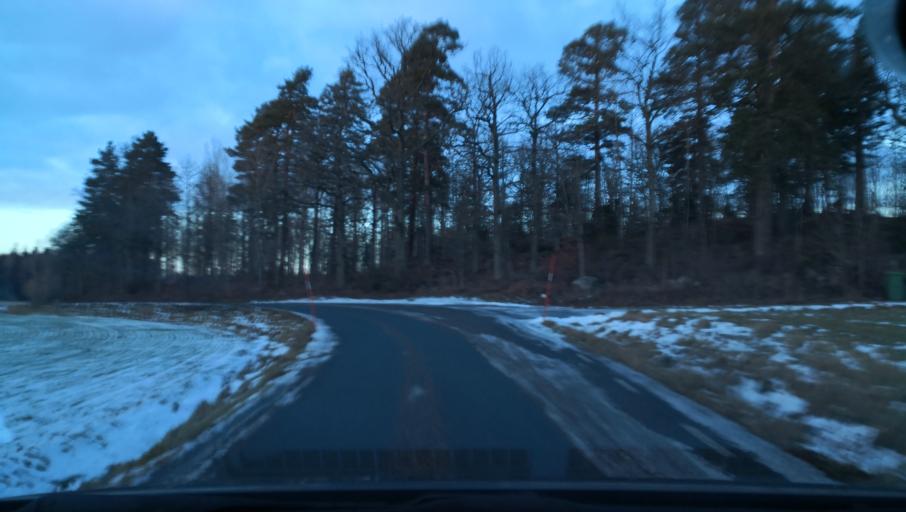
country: SE
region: Soedermanland
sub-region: Eskilstuna Kommun
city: Skogstorp
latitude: 59.2315
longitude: 16.3346
